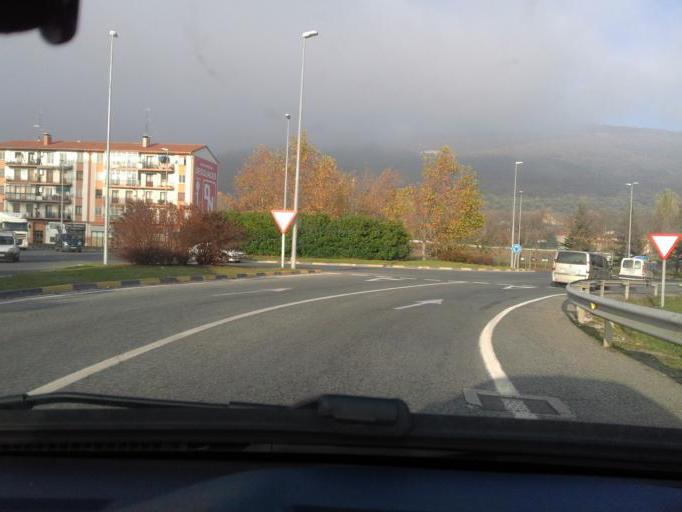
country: ES
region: Navarre
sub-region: Provincia de Navarra
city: Berriozar
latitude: 42.8416
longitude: -1.6813
